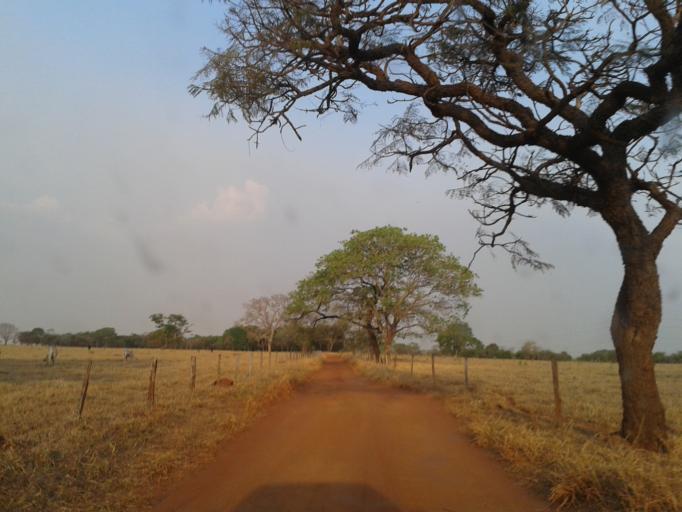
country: BR
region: Minas Gerais
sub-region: Capinopolis
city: Capinopolis
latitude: -18.8059
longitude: -49.7486
